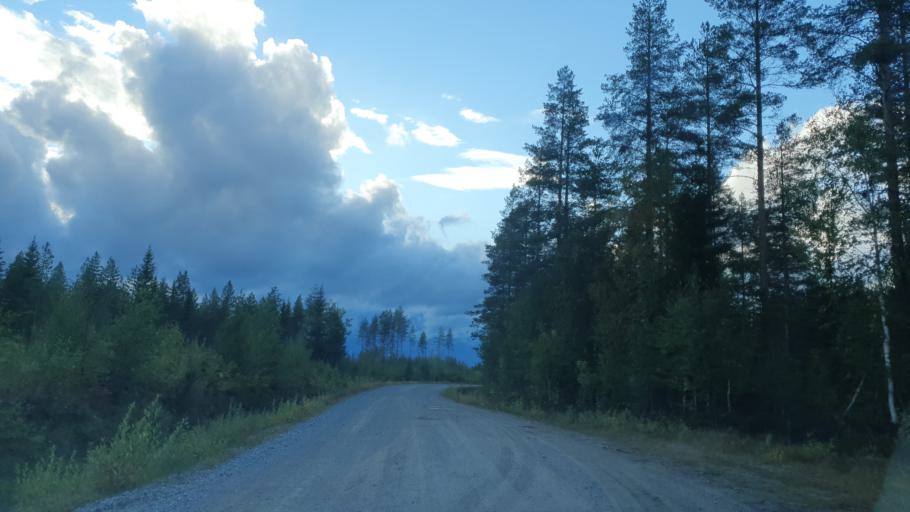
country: FI
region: Kainuu
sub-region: Kehys-Kainuu
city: Kuhmo
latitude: 64.3353
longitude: 29.9335
